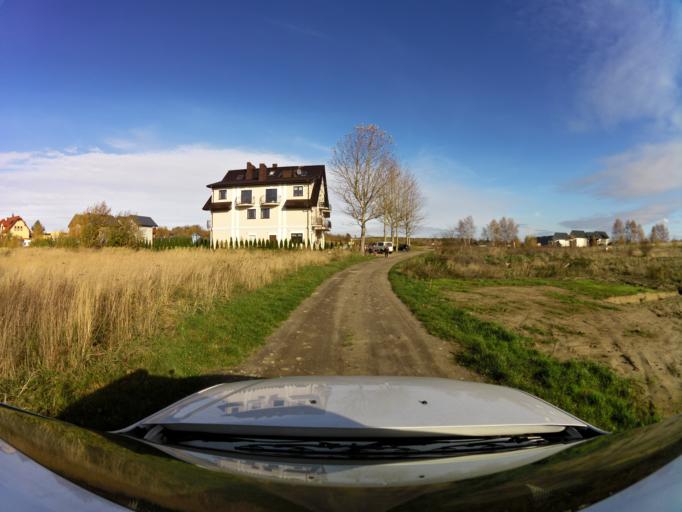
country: PL
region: West Pomeranian Voivodeship
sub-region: Powiat gryficki
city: Rewal
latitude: 54.0827
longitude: 15.0371
